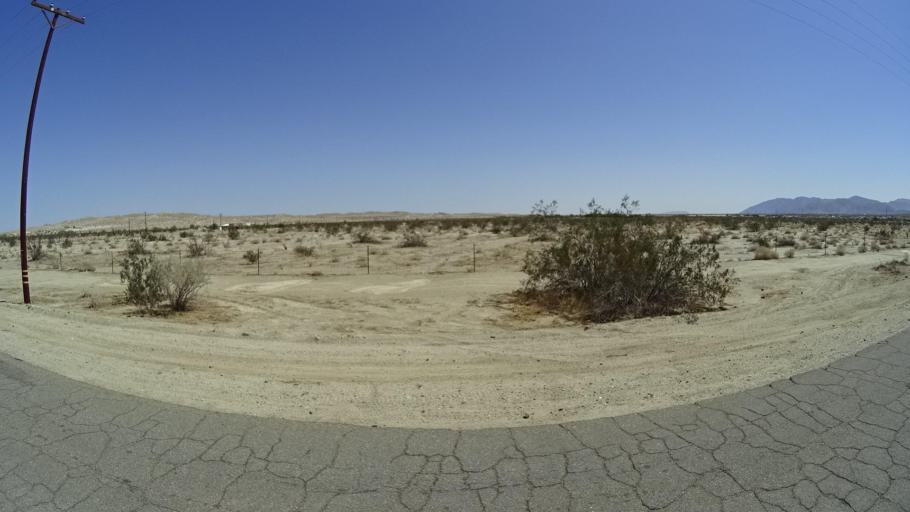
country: US
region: California
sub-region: Imperial County
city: Salton City
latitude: 33.1099
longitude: -116.1328
